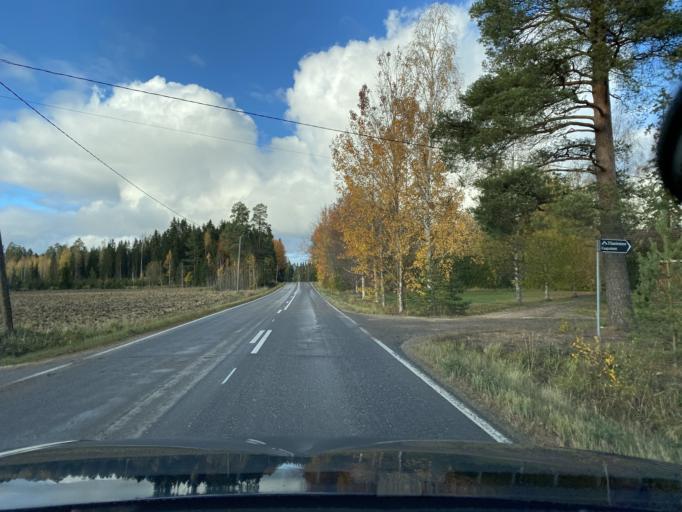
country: FI
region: Haeme
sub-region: Forssa
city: Humppila
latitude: 61.0148
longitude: 23.2529
